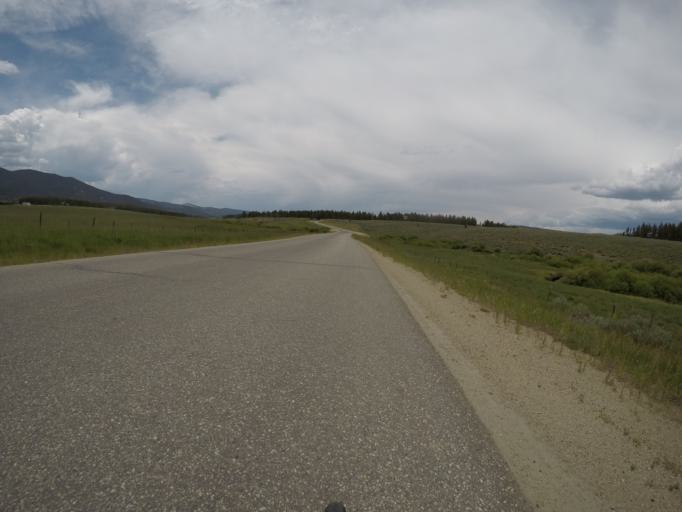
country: US
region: Colorado
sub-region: Grand County
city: Fraser
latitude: 39.9831
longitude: -105.8716
